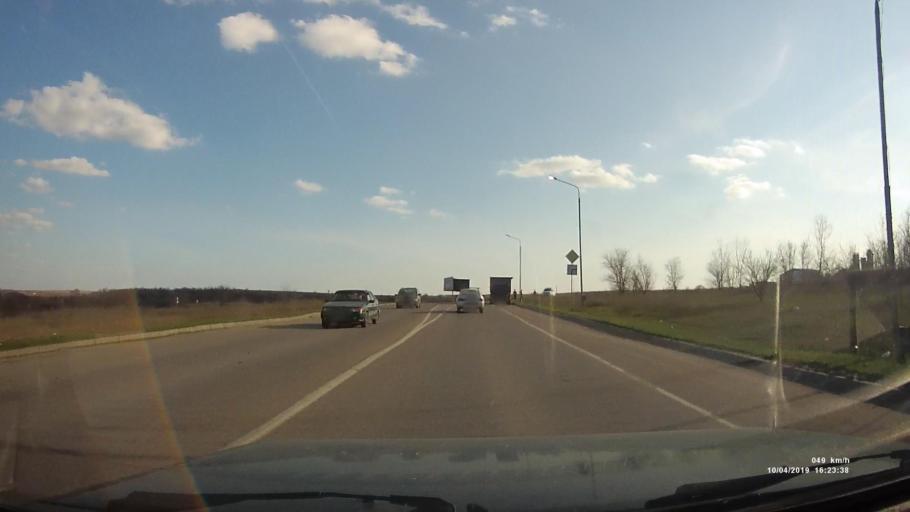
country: RU
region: Rostov
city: Staraya Stanitsa
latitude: 48.3030
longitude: 40.3097
